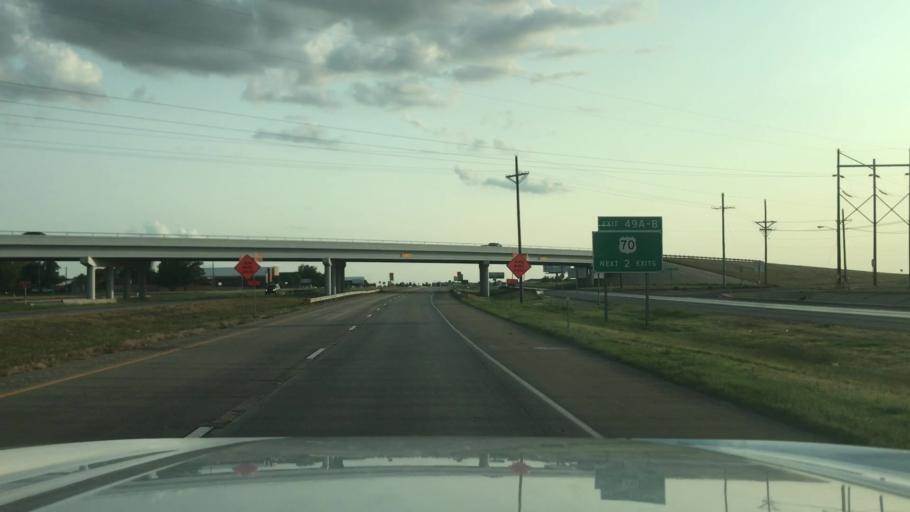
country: US
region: Texas
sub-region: Hale County
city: Plainview
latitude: 34.2051
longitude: -101.7413
